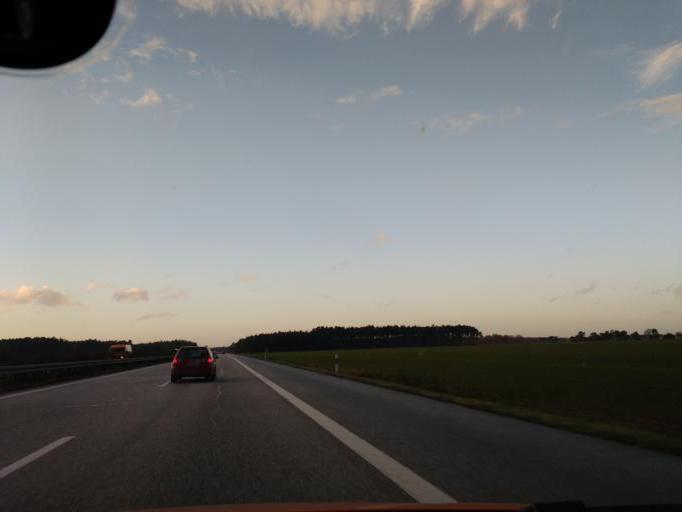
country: DE
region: Mecklenburg-Vorpommern
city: Sulstorf
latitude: 53.4496
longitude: 11.3651
